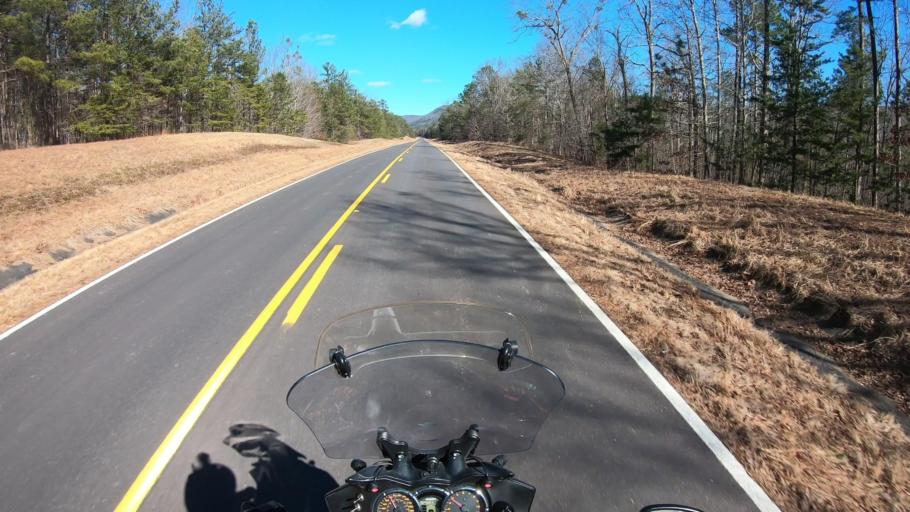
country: US
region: Alabama
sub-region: Talladega County
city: Munford
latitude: 33.4273
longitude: -85.8561
